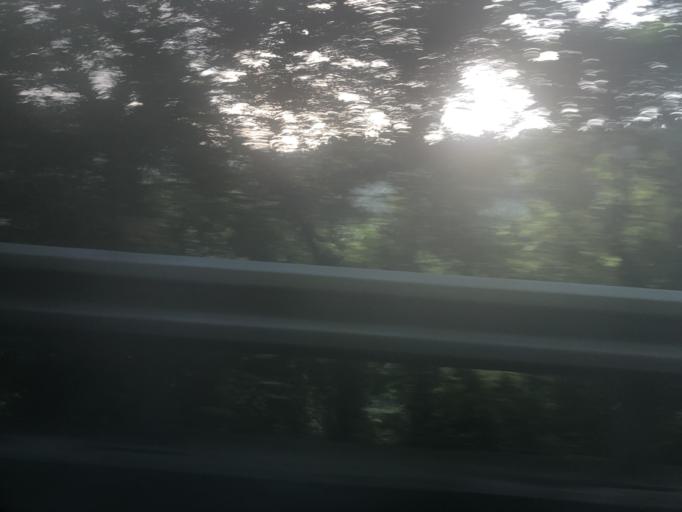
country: TW
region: Taiwan
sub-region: Keelung
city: Keelung
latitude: 25.1693
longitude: 121.6597
